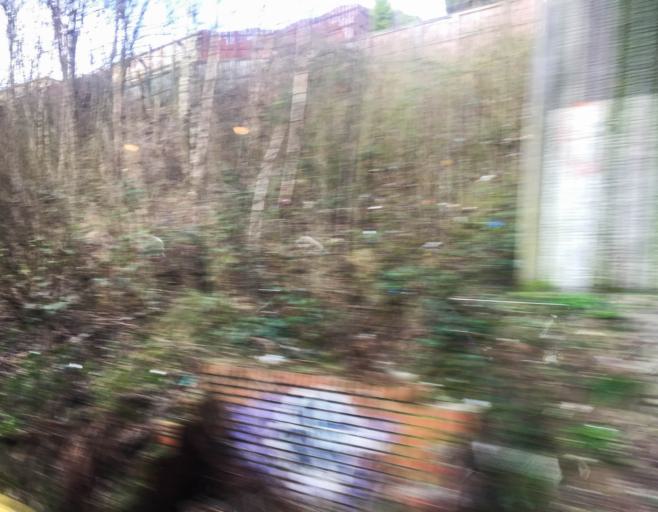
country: GB
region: Scotland
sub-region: West Dunbartonshire
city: Old Kilpatrick
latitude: 55.9206
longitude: -4.4468
